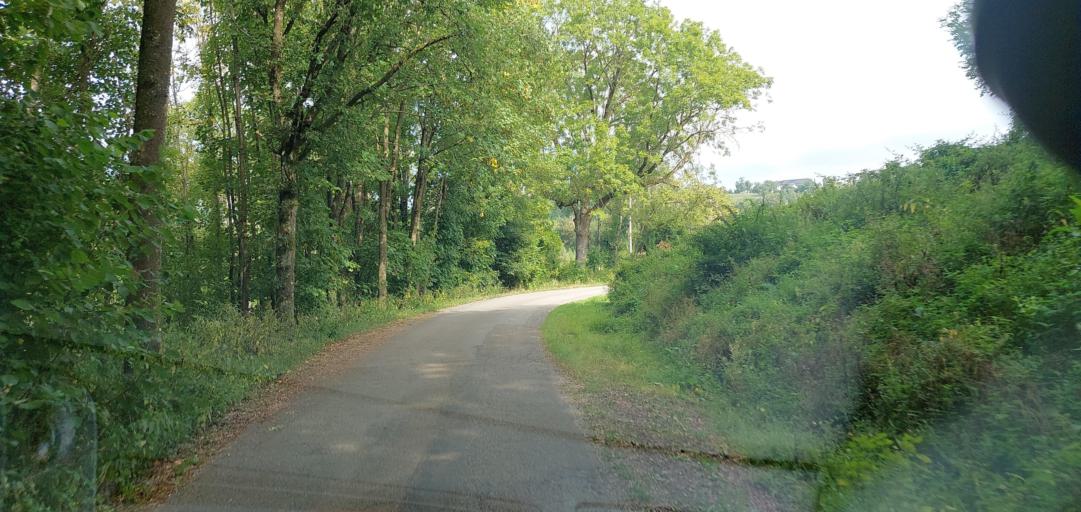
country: AT
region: Upper Austria
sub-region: Politischer Bezirk Urfahr-Umgebung
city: Feldkirchen an der Donau
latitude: 48.3258
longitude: 13.9863
